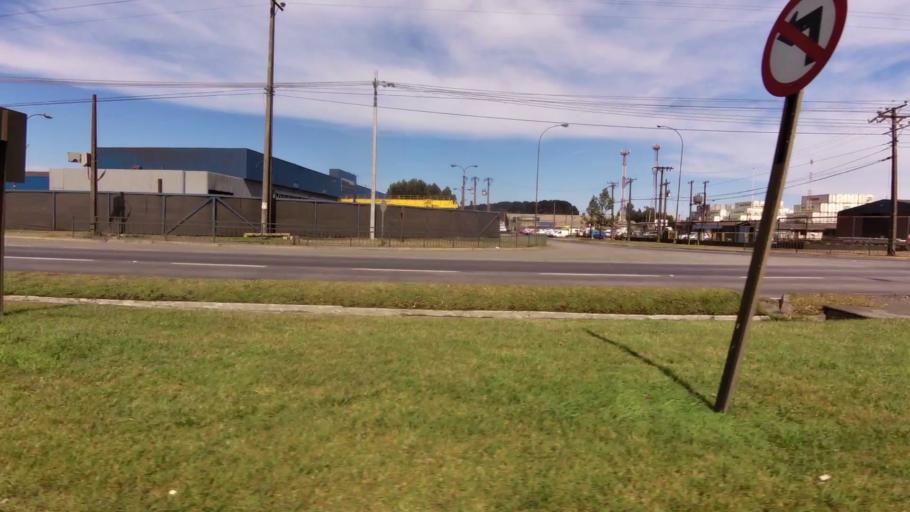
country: CL
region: Biobio
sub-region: Provincia de Concepcion
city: Talcahuano
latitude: -36.7557
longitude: -73.1228
